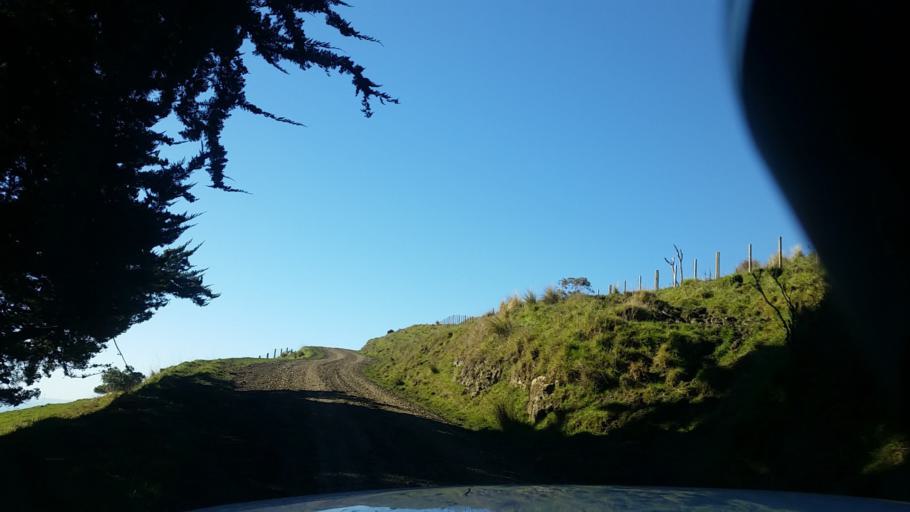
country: NZ
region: Canterbury
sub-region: Christchurch City
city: Christchurch
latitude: -43.6623
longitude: 172.9954
